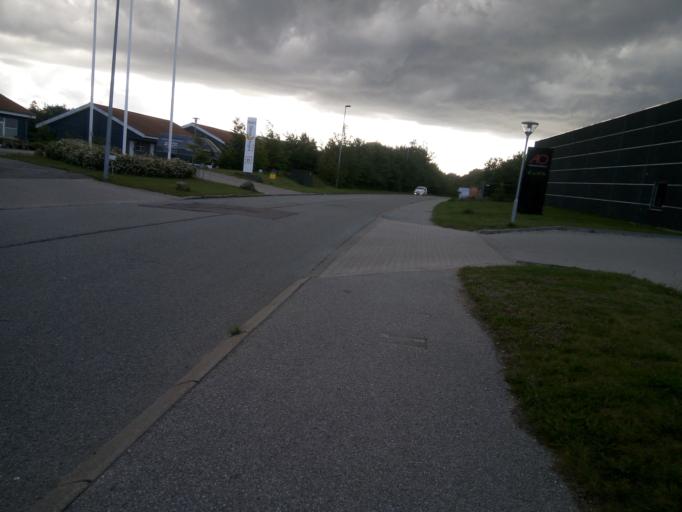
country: DK
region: Capital Region
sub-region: Helsingor Kommune
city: Espergaerde
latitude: 56.0216
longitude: 12.5661
